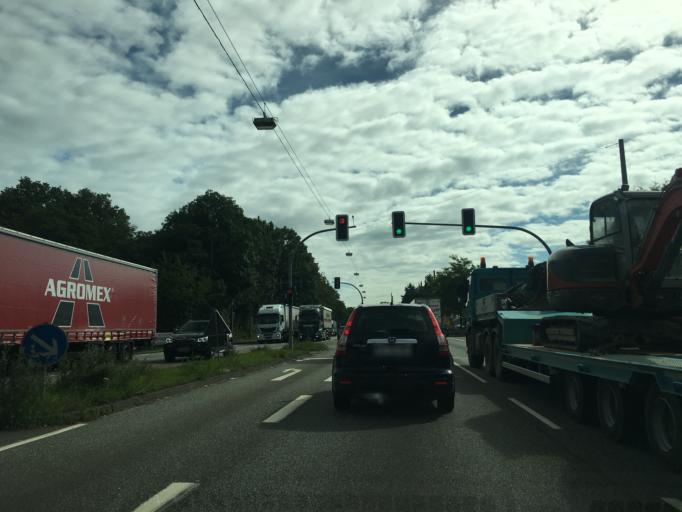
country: DE
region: North Rhine-Westphalia
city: Bad Oeynhausen
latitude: 52.2063
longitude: 8.7902
